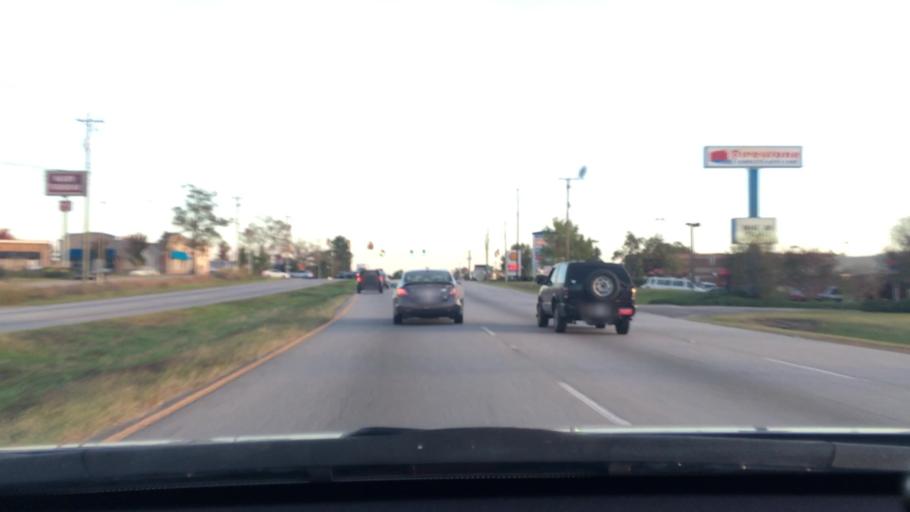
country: US
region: South Carolina
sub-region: Richland County
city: Forest Acres
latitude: 33.9642
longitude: -80.9428
